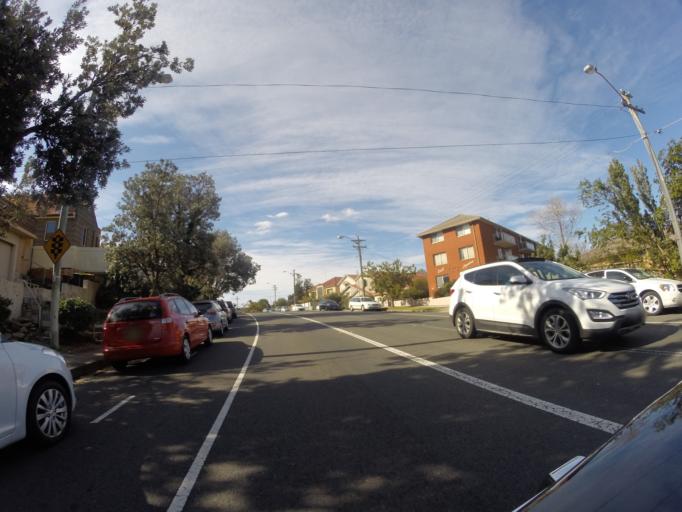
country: AU
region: New South Wales
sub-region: Randwick
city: South Coogee
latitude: -33.9400
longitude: 151.2557
